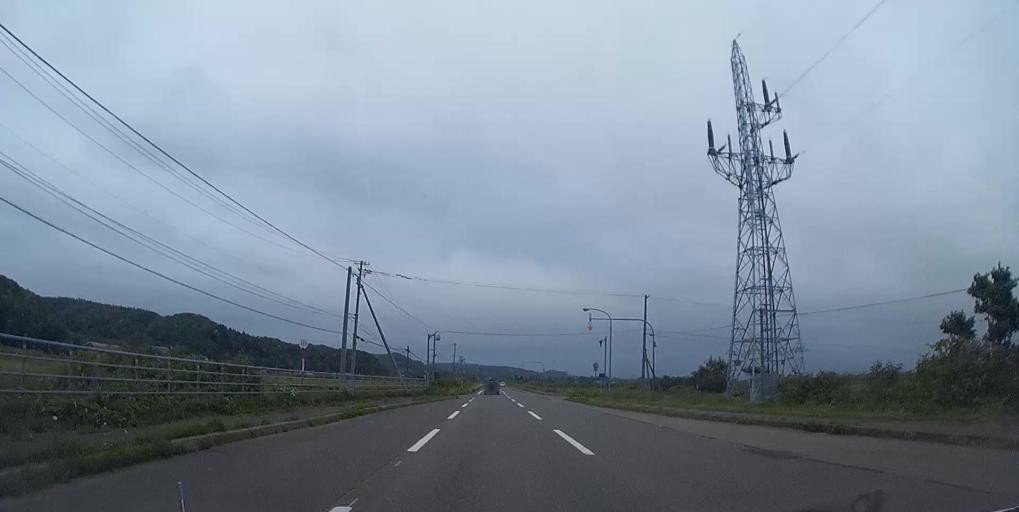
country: JP
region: Hokkaido
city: Iwanai
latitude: 42.4266
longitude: 139.9109
